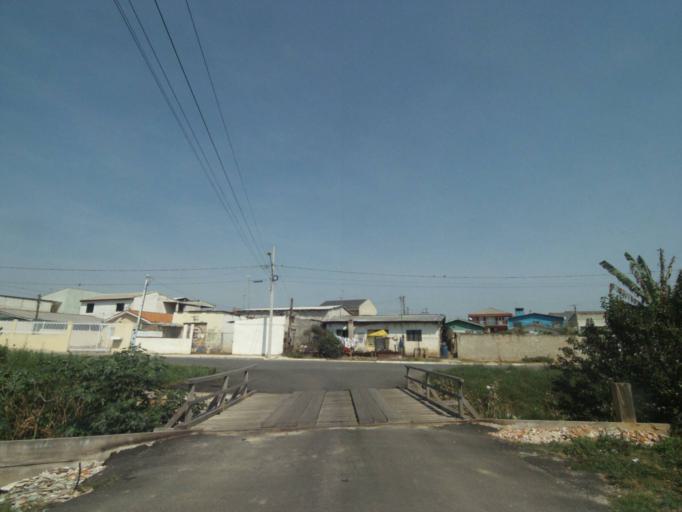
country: BR
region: Parana
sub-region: Curitiba
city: Curitiba
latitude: -25.4838
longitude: -49.3070
